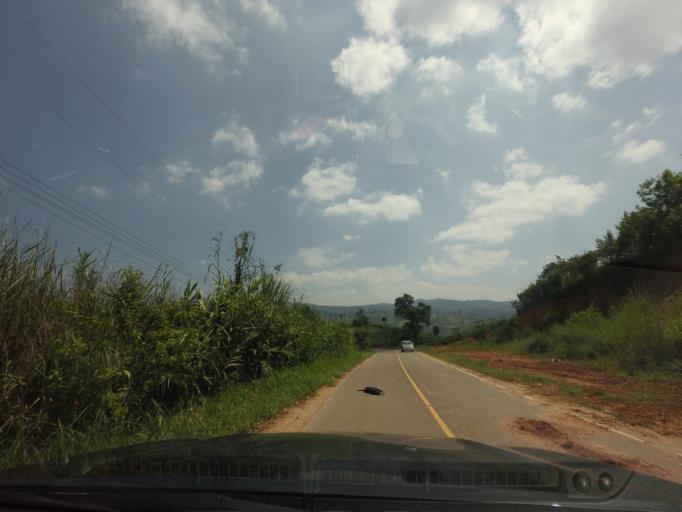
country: TH
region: Loei
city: Na Haeo
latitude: 17.5263
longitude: 100.8786
